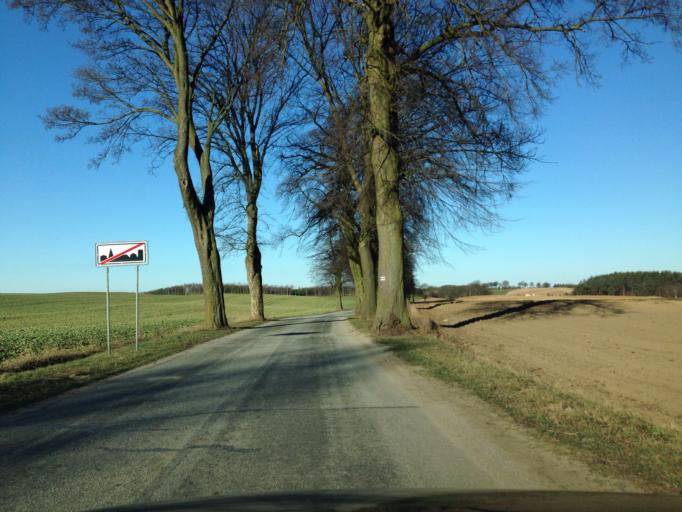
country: PL
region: Kujawsko-Pomorskie
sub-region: Powiat brodnicki
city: Brzozie
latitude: 53.2943
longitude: 19.6559
